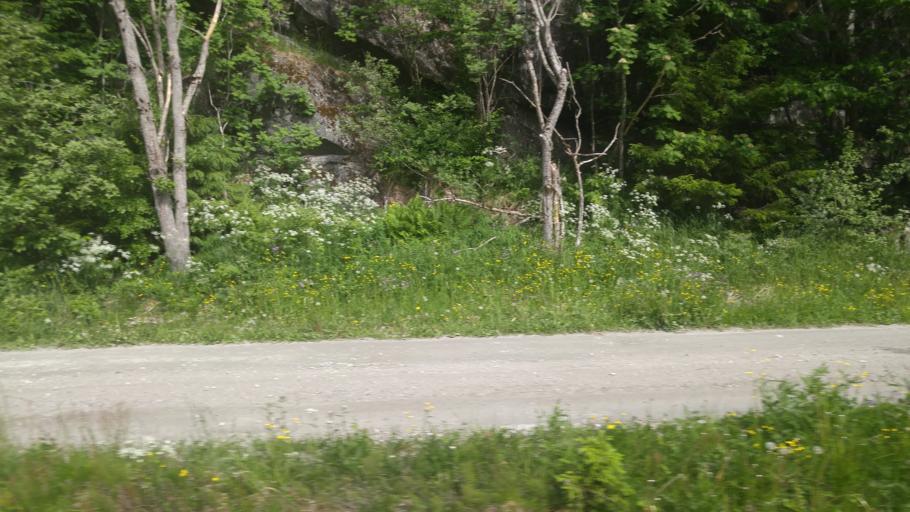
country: NO
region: Sor-Trondelag
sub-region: Midtre Gauldal
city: Storen
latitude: 63.0198
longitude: 10.4187
